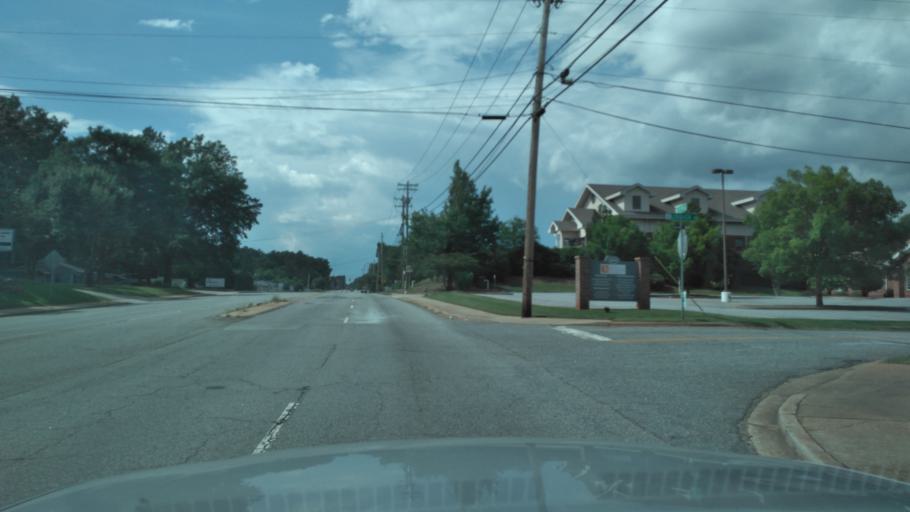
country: US
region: South Carolina
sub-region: Spartanburg County
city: Spartanburg
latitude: 34.9770
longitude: -81.9425
